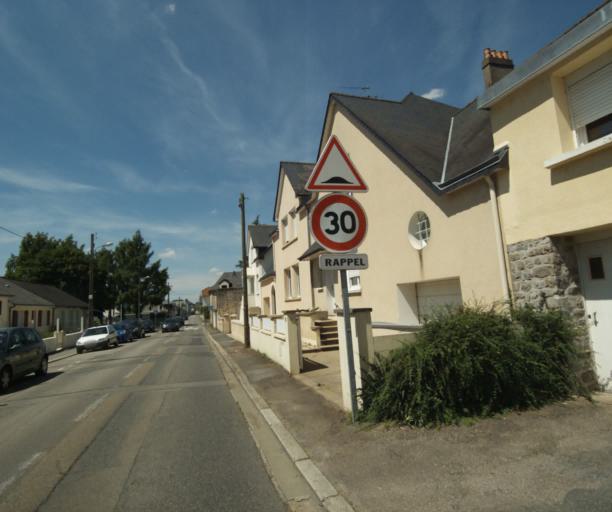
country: FR
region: Pays de la Loire
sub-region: Departement de la Mayenne
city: Laval
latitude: 48.0779
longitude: -0.7661
